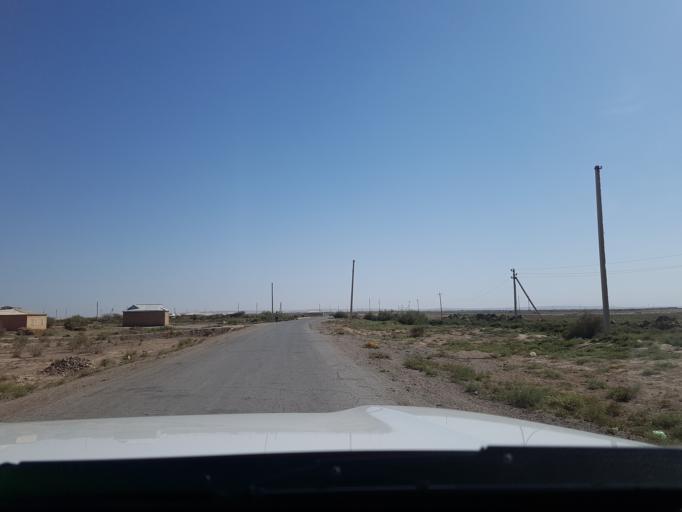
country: IR
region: Razavi Khorasan
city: Sarakhs
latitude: 36.5151
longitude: 61.2526
